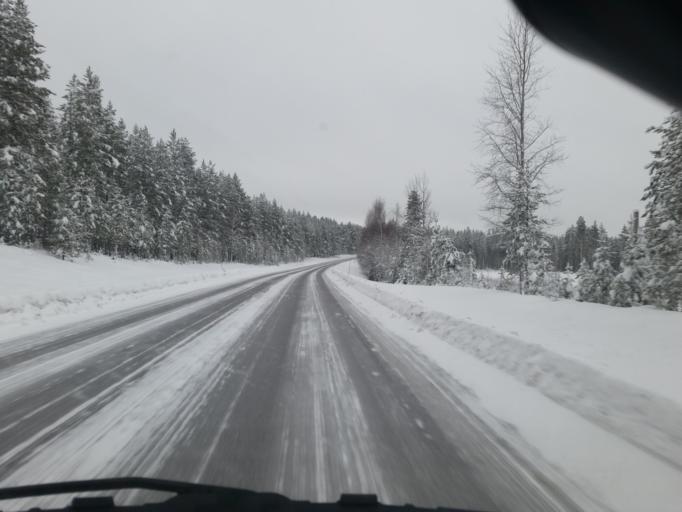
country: SE
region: Norrbotten
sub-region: Pitea Kommun
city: Roknas
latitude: 65.4145
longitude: 21.3004
